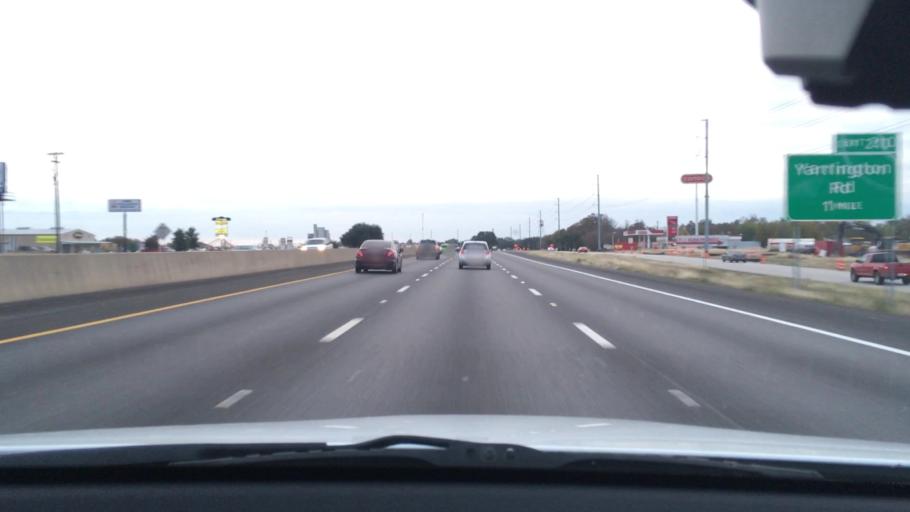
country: US
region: Texas
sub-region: Hays County
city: Kyle
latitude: 30.0005
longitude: -97.8683
